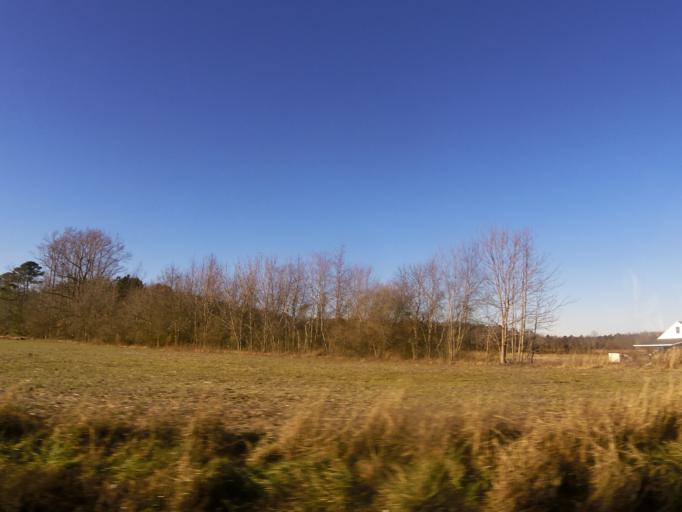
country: US
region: Virginia
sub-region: Isle of Wight County
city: Windsor
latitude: 36.6945
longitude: -76.7315
